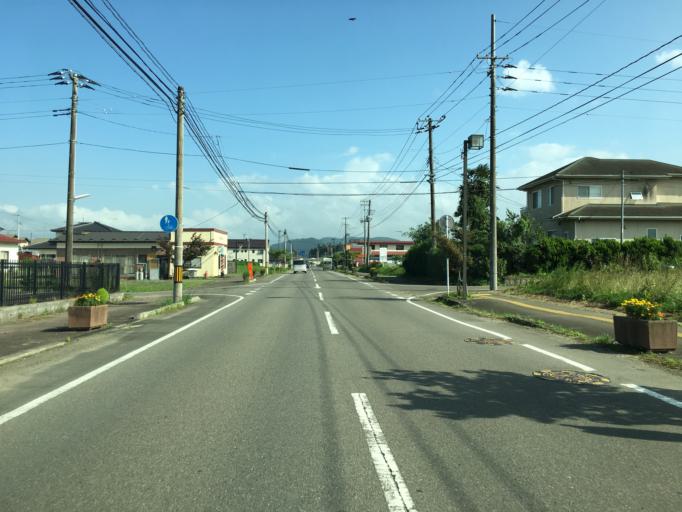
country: JP
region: Miyagi
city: Marumori
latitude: 37.9288
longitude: 140.7630
